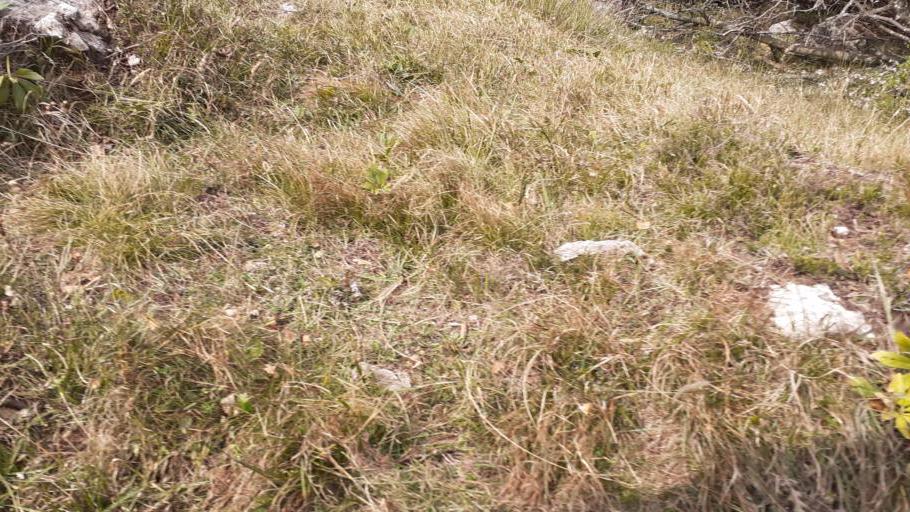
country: IT
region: Lombardy
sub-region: Provincia di Lecco
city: Ballabio
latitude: 45.9145
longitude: 9.3999
